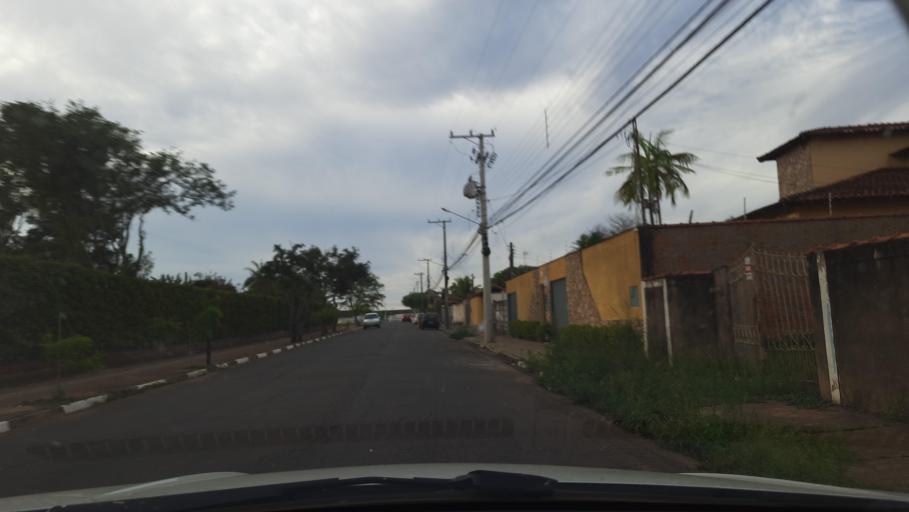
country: BR
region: Sao Paulo
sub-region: Casa Branca
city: Casa Branca
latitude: -21.7804
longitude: -47.0673
